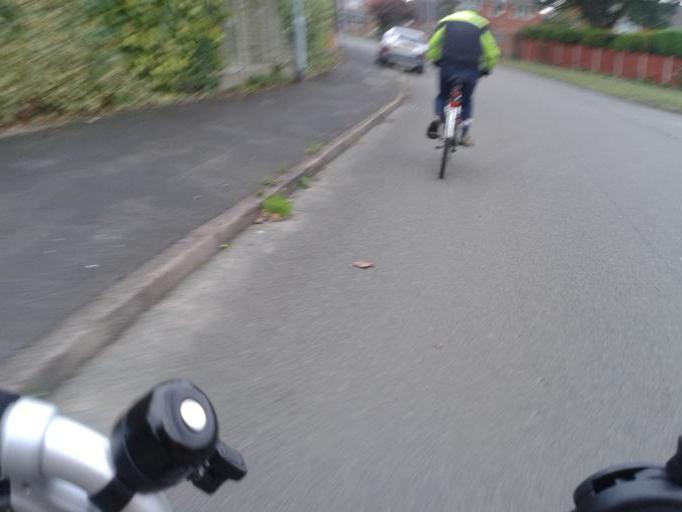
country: GB
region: England
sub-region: Leicestershire
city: Hinckley
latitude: 52.5555
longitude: -1.3590
